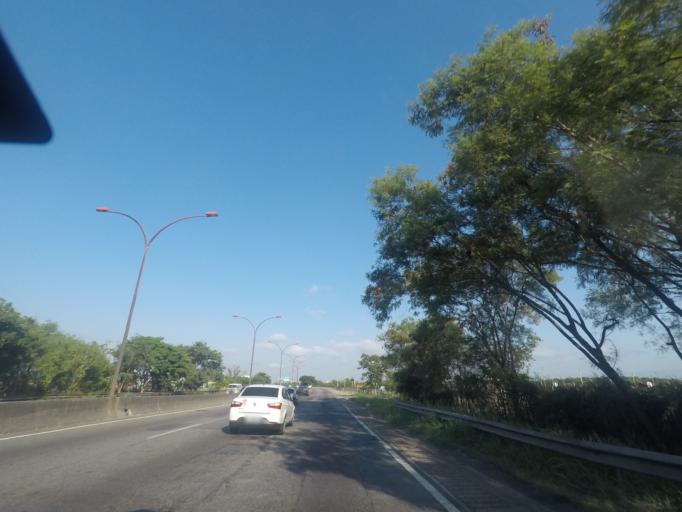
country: BR
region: Rio de Janeiro
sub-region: Duque De Caxias
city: Duque de Caxias
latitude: -22.8087
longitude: -43.2745
